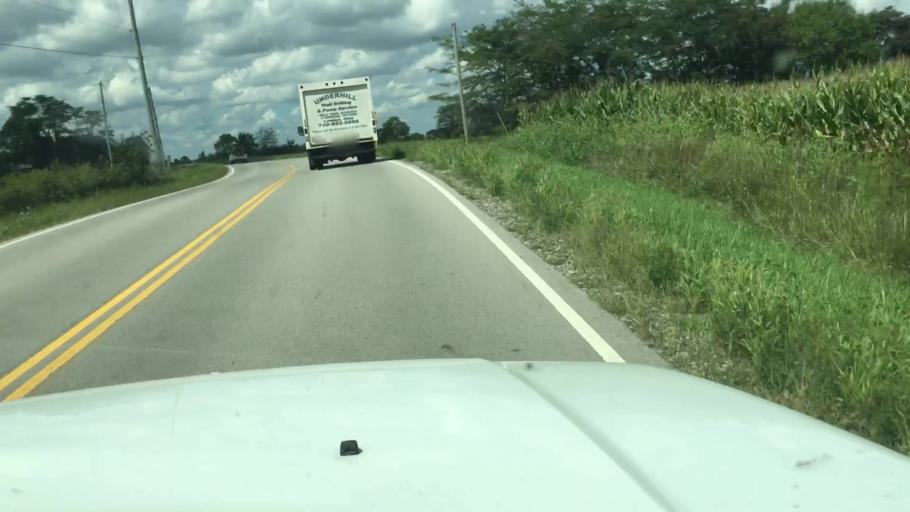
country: US
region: Ohio
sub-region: Madison County
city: Bethel
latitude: 39.8250
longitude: -83.3616
